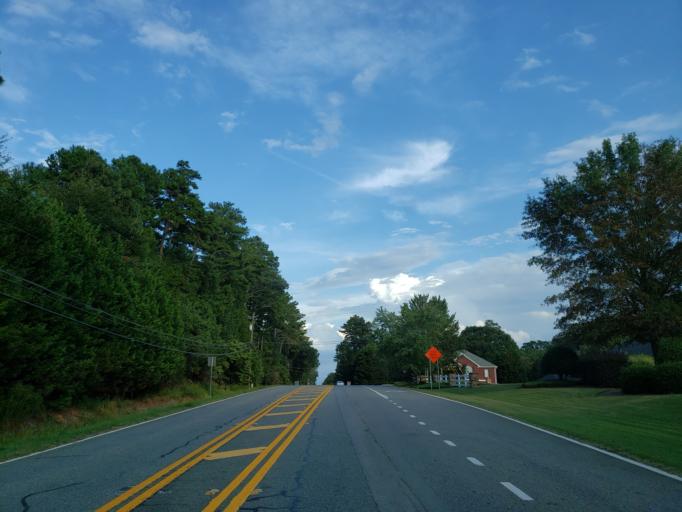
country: US
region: Georgia
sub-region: Bartow County
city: Cartersville
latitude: 34.2396
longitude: -84.8776
